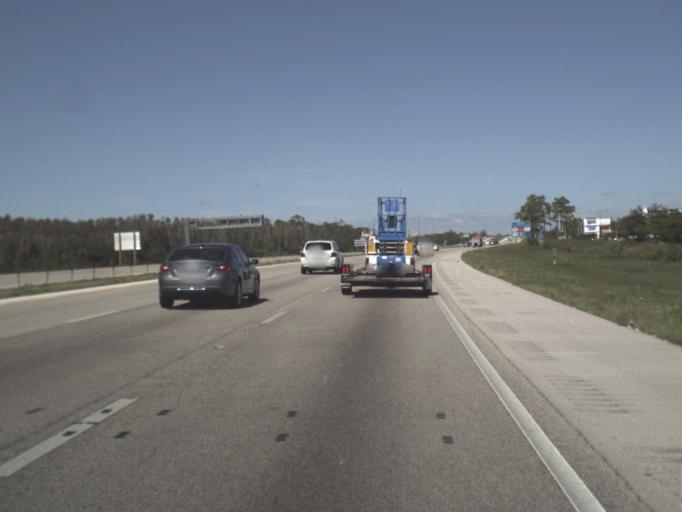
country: US
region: Florida
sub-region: Lee County
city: Fort Myers
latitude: 26.6253
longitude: -81.8054
